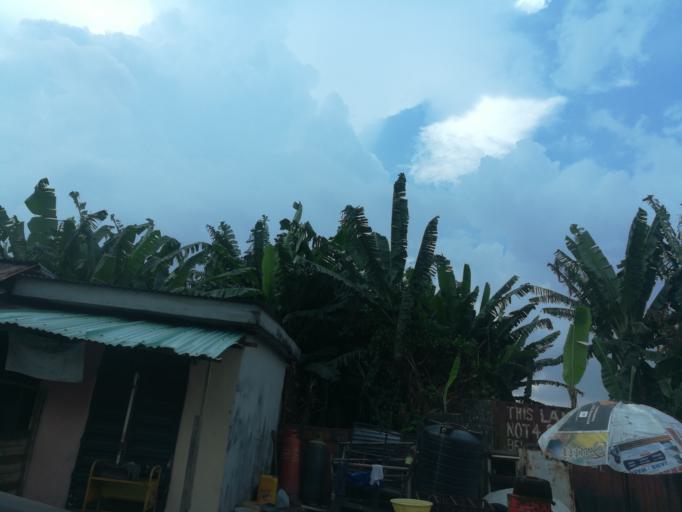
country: NG
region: Lagos
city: Ikeja
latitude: 6.6036
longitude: 3.3634
